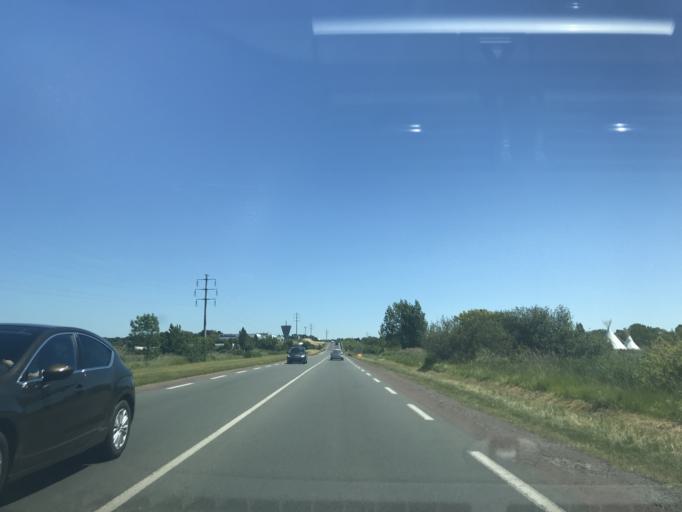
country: FR
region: Poitou-Charentes
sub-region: Departement de la Charente-Maritime
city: Royan
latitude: 45.6331
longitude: -1.0110
